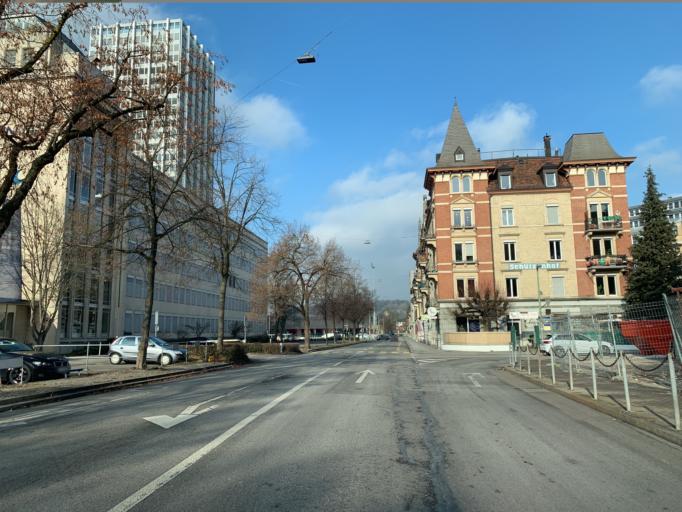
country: CH
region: Zurich
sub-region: Bezirk Winterthur
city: Stadt Winterthur (Kreis 1)
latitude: 47.4989
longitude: 8.7200
